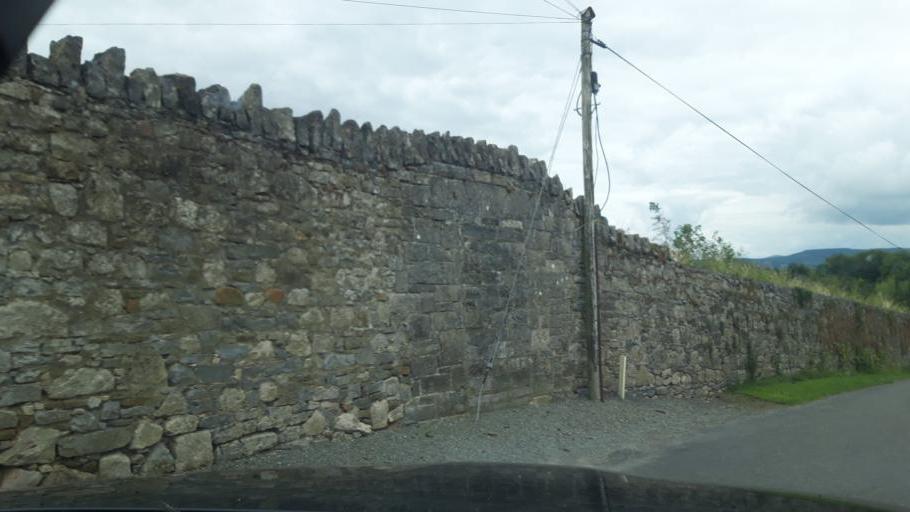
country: IE
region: Leinster
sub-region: Kilkenny
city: Thomastown
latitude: 52.6282
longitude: -7.0660
